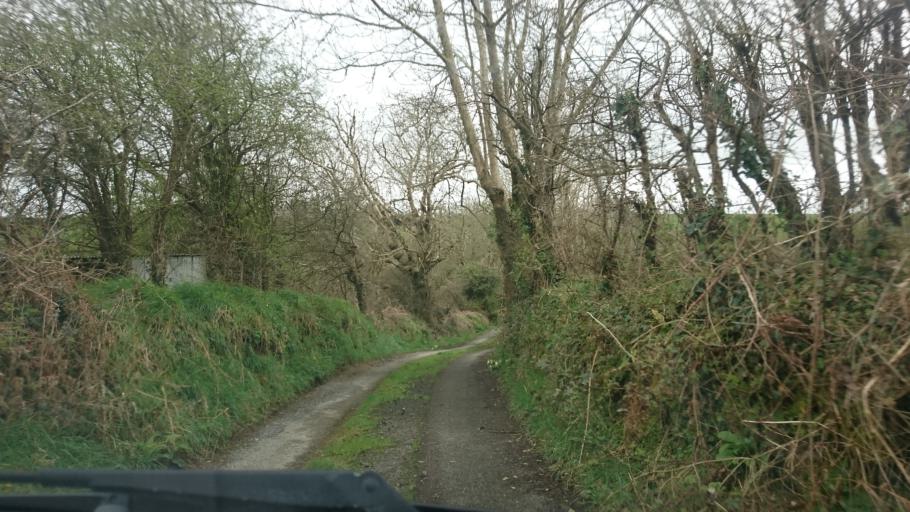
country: IE
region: Munster
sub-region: Waterford
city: Waterford
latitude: 52.2268
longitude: -7.0366
